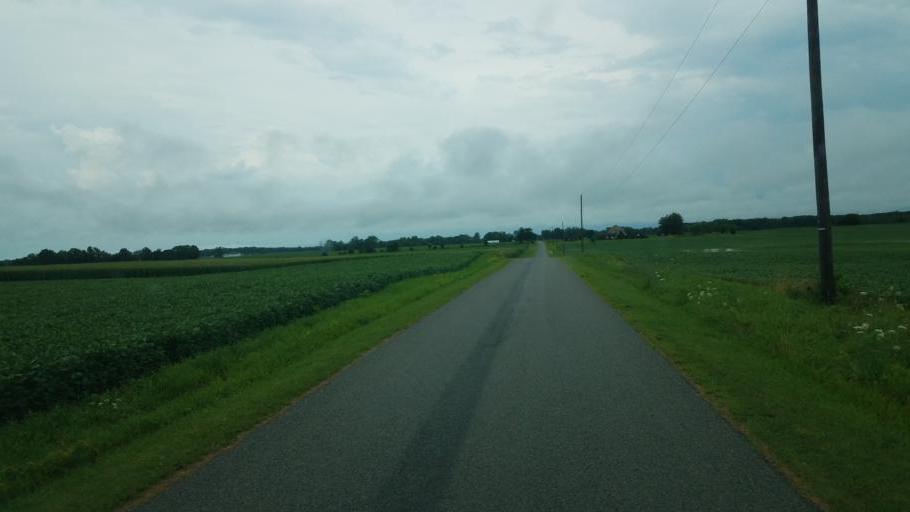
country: US
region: Ohio
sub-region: Union County
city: Richwood
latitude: 40.4959
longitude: -83.3026
